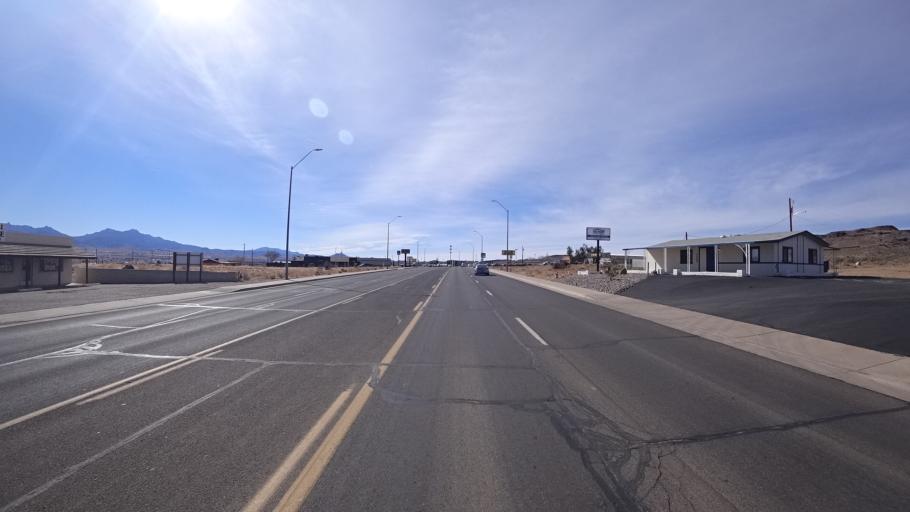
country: US
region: Arizona
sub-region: Mohave County
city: New Kingman-Butler
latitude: 35.2527
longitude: -114.0384
